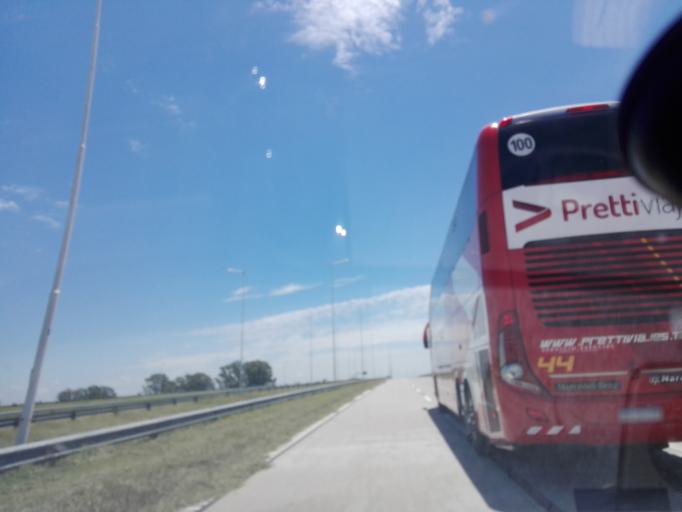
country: AR
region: Cordoba
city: Villa Maria
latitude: -32.4203
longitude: -63.1560
